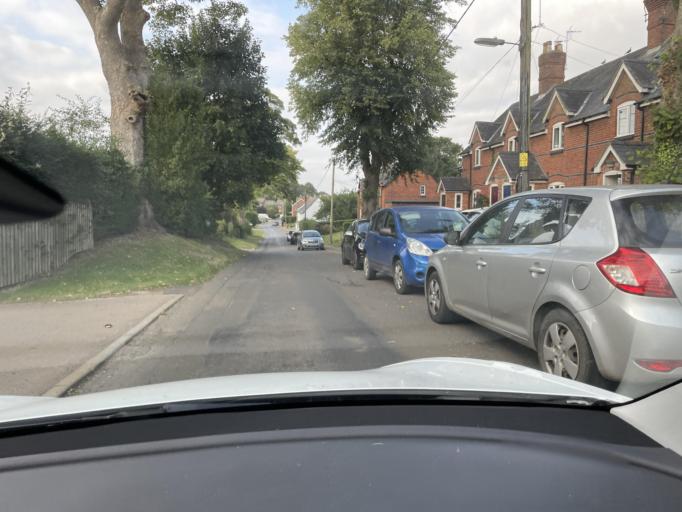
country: GB
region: England
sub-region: Northamptonshire
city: Brixworth
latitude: 52.3929
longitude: -0.9897
